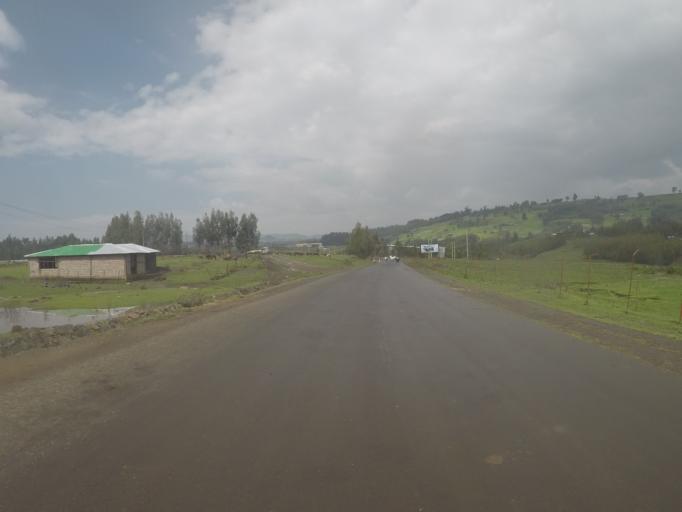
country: ET
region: Amhara
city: Debark'
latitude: 13.1275
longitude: 37.8878
